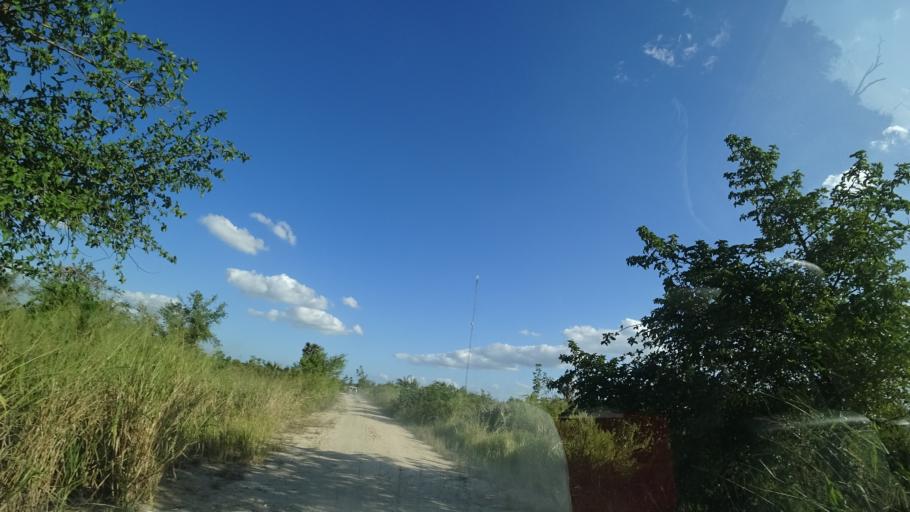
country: MZ
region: Sofala
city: Dondo
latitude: -19.3770
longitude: 34.5919
